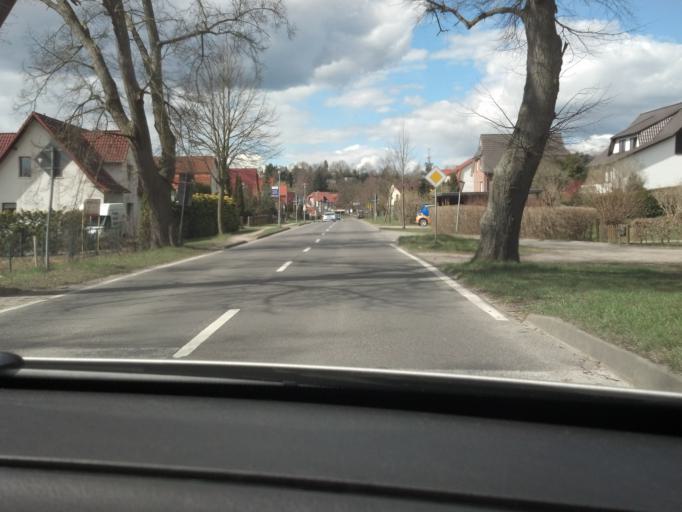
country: DE
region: Mecklenburg-Vorpommern
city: Burg Stargard
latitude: 53.4922
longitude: 13.3240
